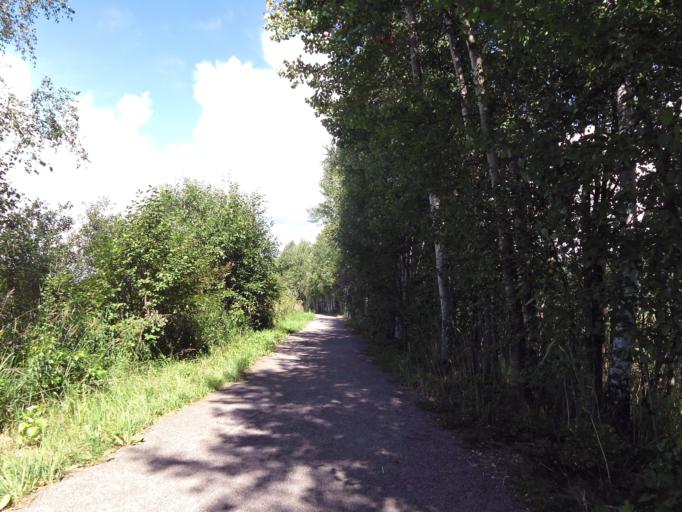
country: FI
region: Uusimaa
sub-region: Helsinki
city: Koukkuniemi
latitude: 60.1524
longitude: 24.7223
